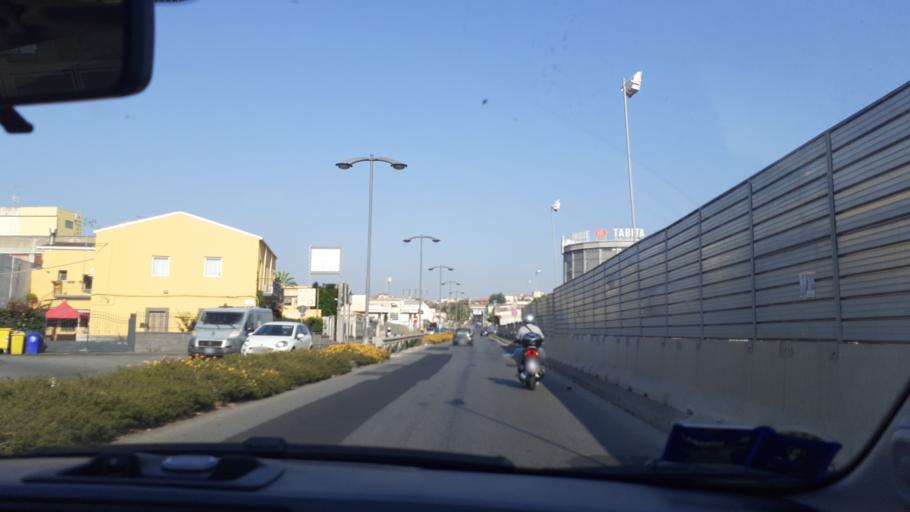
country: IT
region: Sicily
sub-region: Catania
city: Misterbianco
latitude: 37.5139
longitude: 15.0263
